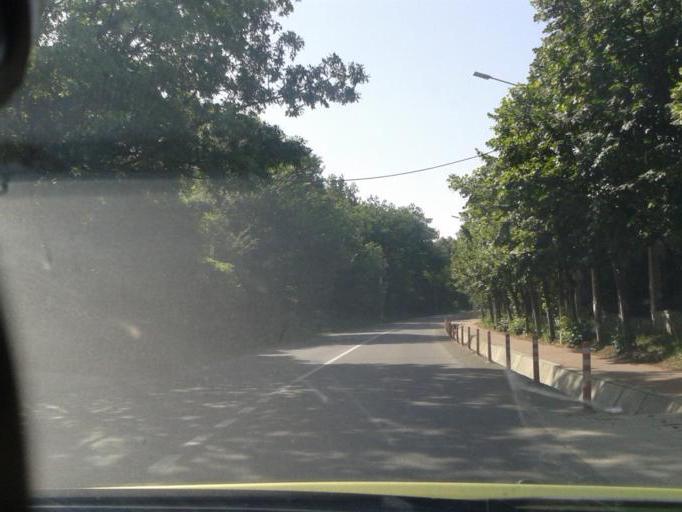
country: RO
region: Prahova
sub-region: Comuna Paulesti
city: Gageni
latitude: 45.0144
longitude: 25.9509
